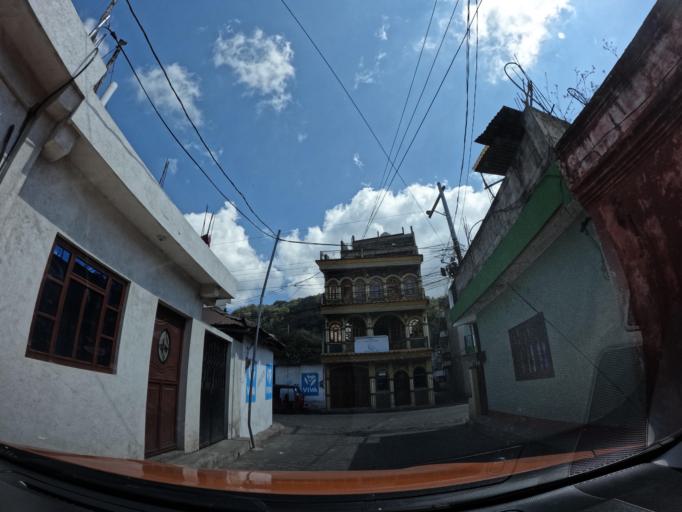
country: GT
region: Solola
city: Santiago Atitlan
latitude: 14.6349
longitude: -91.2304
